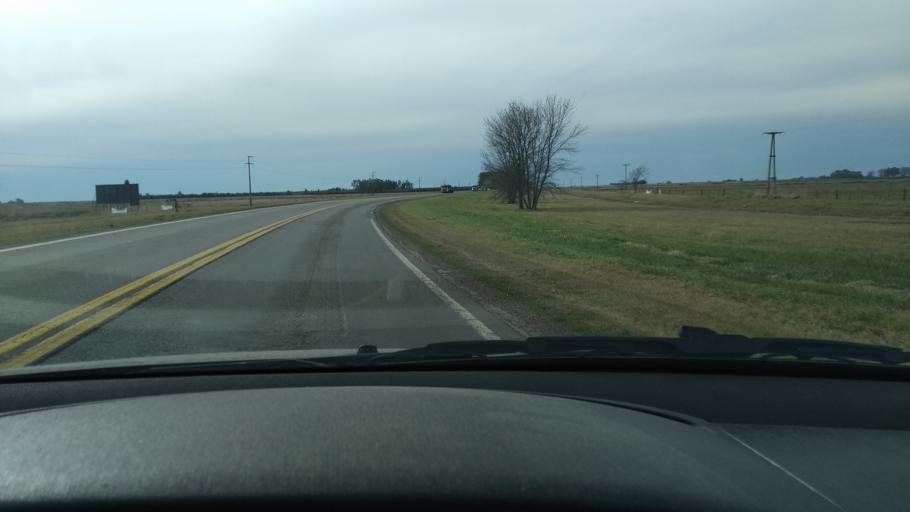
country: AR
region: Buenos Aires
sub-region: Partido de Azul
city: Azul
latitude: -36.7517
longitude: -59.8039
